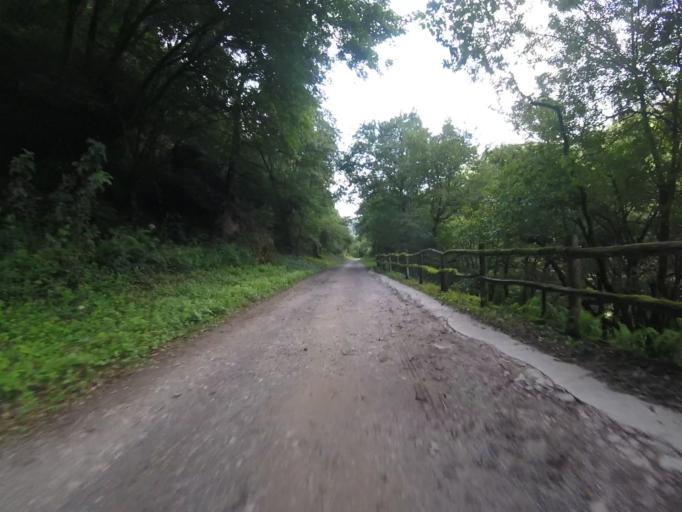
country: ES
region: Basque Country
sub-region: Provincia de Guipuzcoa
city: Elduayen
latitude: 43.1832
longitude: -1.9957
